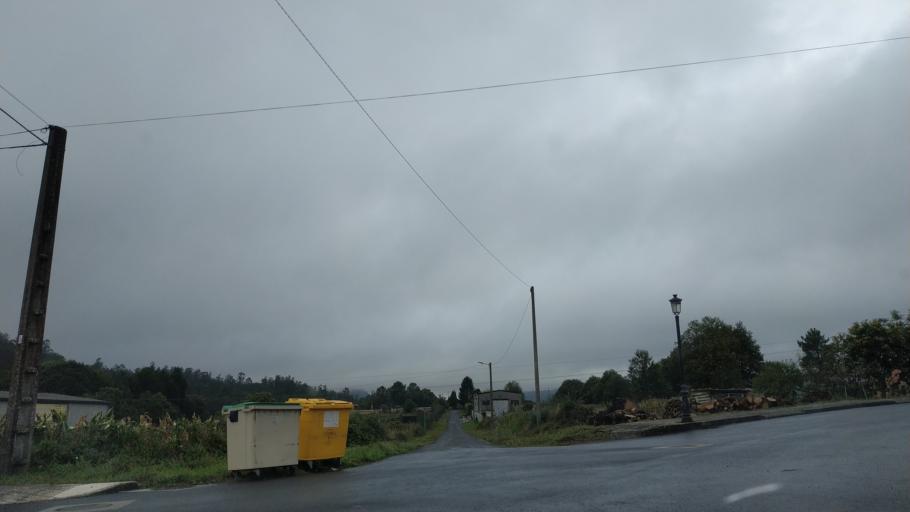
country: ES
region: Galicia
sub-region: Provincia da Coruna
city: Negreira
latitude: 42.9096
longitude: -8.7420
